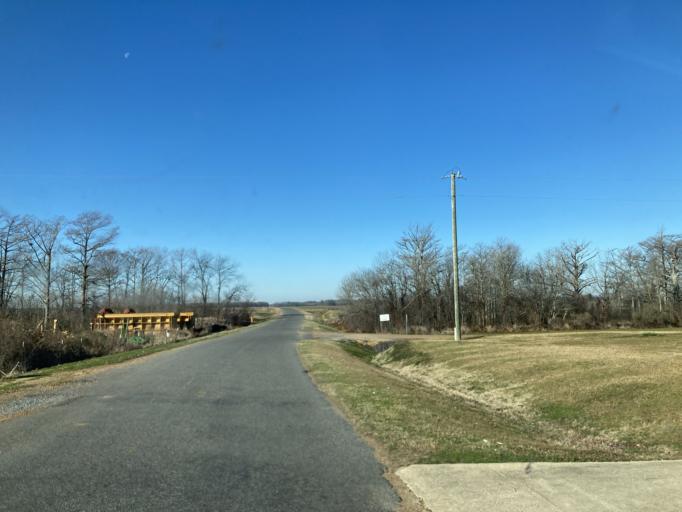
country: US
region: Mississippi
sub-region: Yazoo County
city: Yazoo City
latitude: 32.9518
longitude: -90.5913
